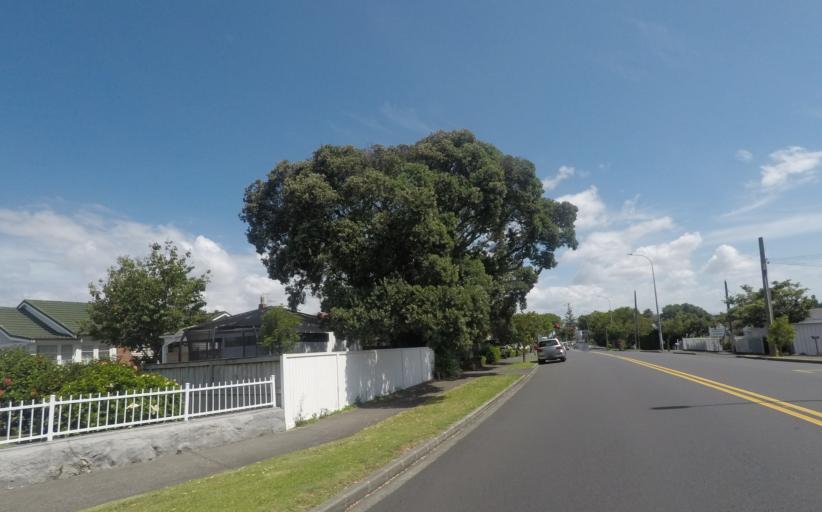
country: NZ
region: Auckland
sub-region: Auckland
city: Tamaki
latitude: -36.8738
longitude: 174.8288
